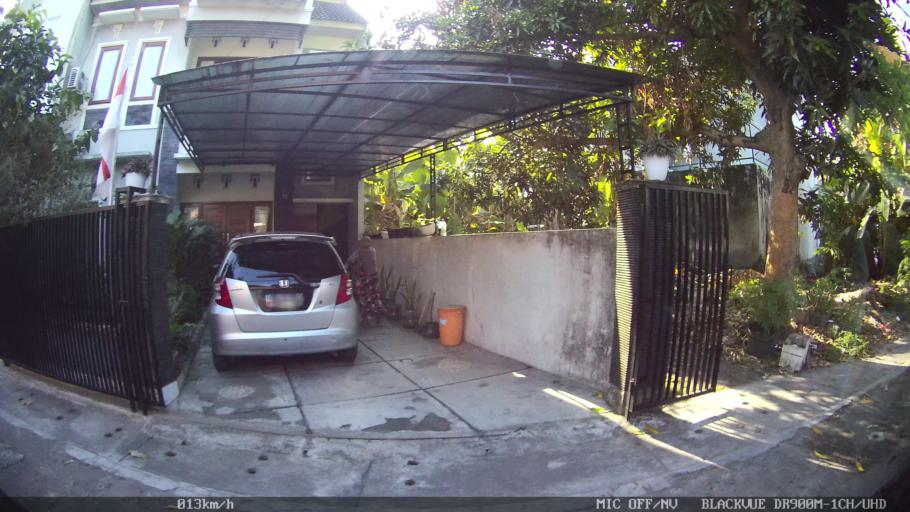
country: ID
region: Daerah Istimewa Yogyakarta
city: Yogyakarta
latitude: -7.8238
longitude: 110.3828
